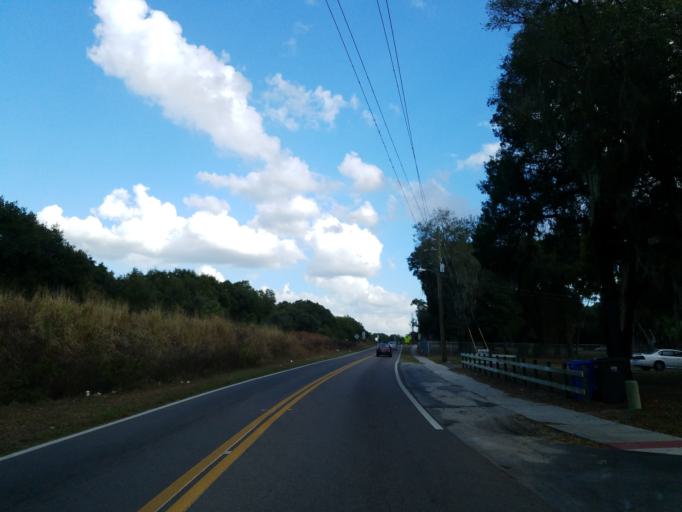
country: US
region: Florida
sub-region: Hillsborough County
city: Brandon
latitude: 27.9451
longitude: -82.2931
